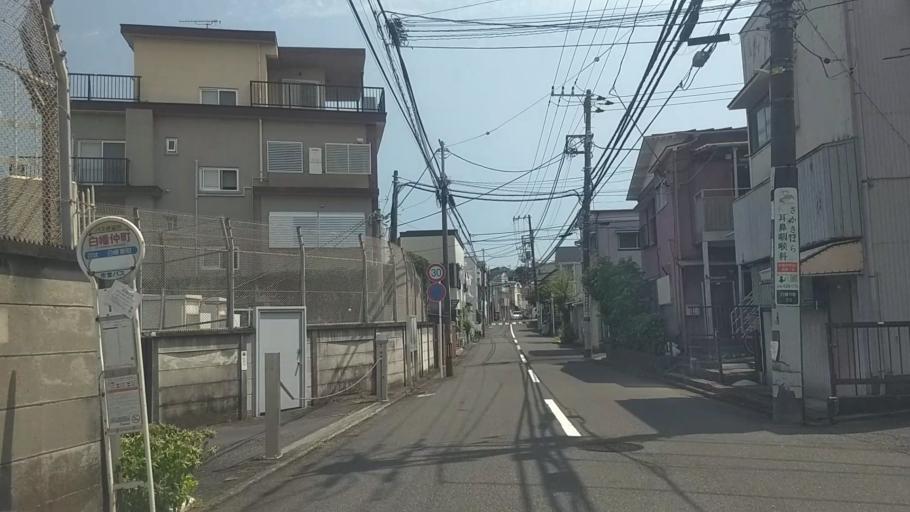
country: JP
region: Kanagawa
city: Yokohama
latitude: 35.4895
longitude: 139.6364
